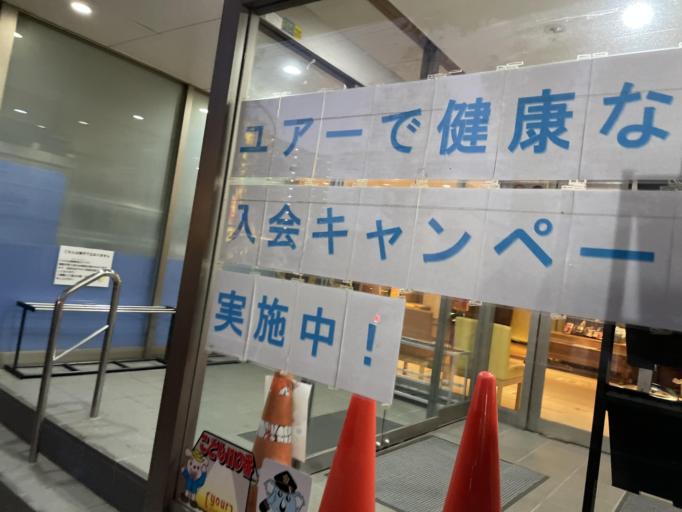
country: JP
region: Chiba
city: Nagareyama
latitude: 35.8234
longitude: 139.9147
